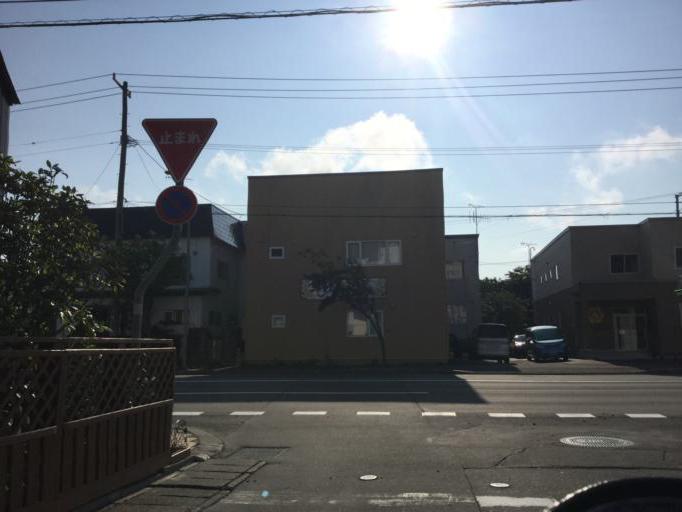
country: JP
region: Hokkaido
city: Wakkanai
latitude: 45.4129
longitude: 141.6758
